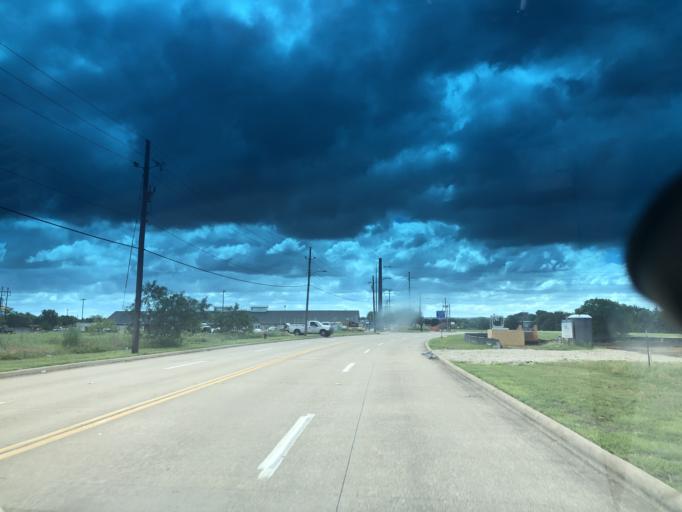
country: US
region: Texas
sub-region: Dallas County
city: Grand Prairie
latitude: 32.6984
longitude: -97.0375
